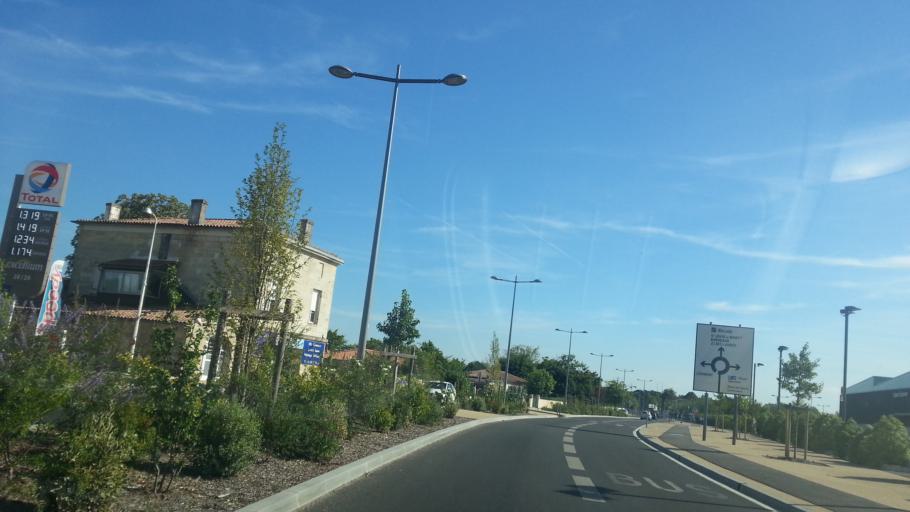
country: FR
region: Aquitaine
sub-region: Departement de la Gironde
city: Bassens
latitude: 44.8901
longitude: -0.5163
